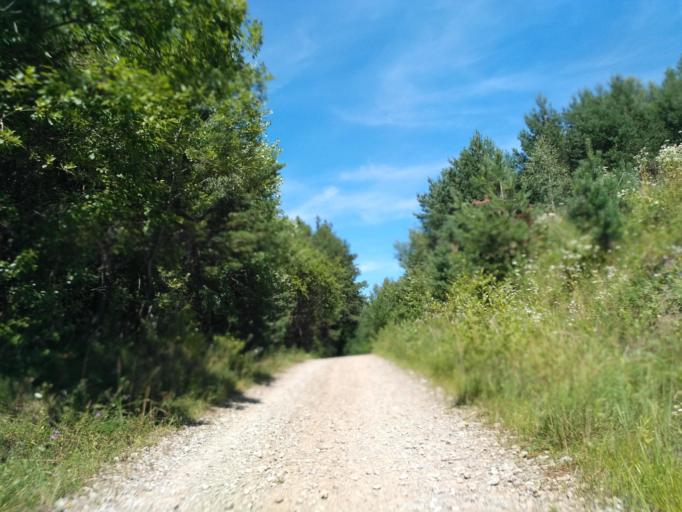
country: PL
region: Subcarpathian Voivodeship
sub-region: Powiat sanocki
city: Bukowsko
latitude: 49.4814
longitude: 22.0922
